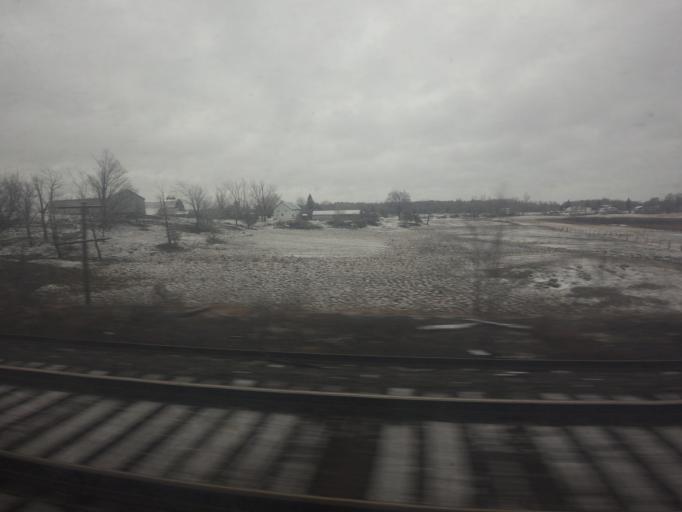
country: CA
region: Ontario
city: Gananoque
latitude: 44.3673
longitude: -76.1653
